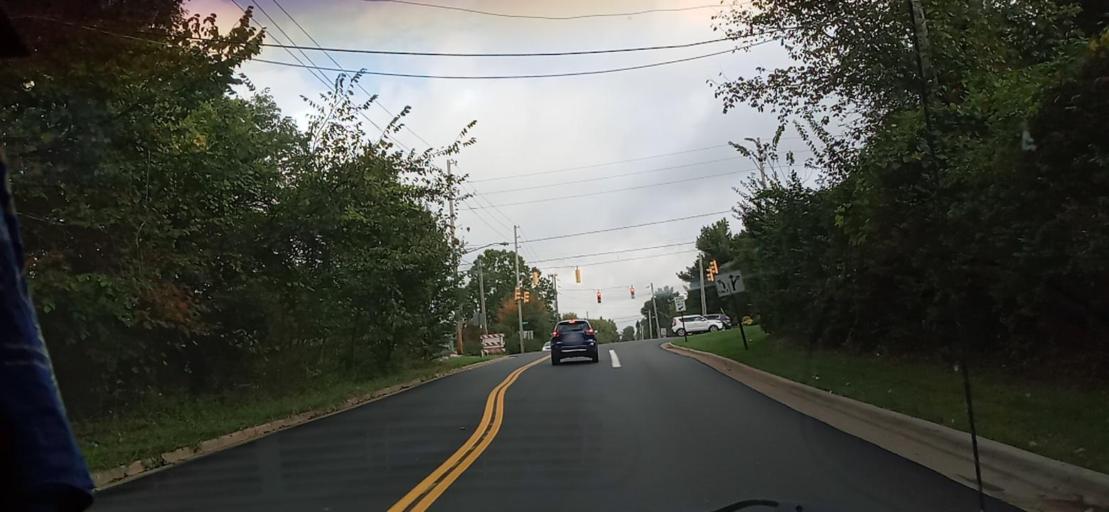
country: US
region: Ohio
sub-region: Summit County
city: Fairlawn
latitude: 41.1397
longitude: -81.5874
